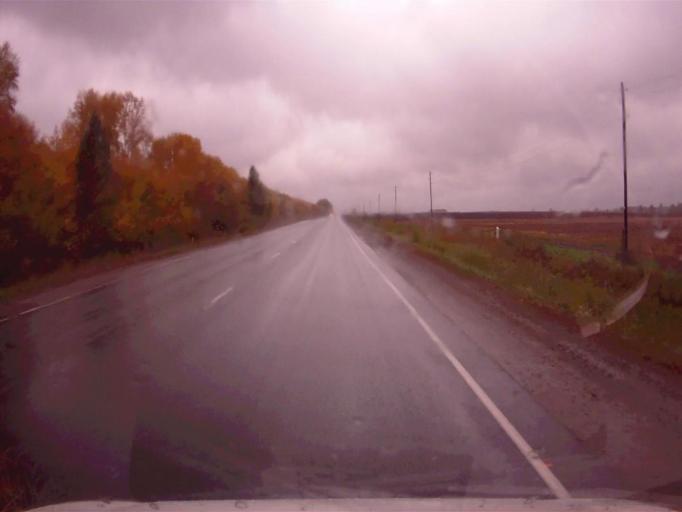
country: RU
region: Chelyabinsk
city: Argayash
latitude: 55.4256
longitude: 61.0034
